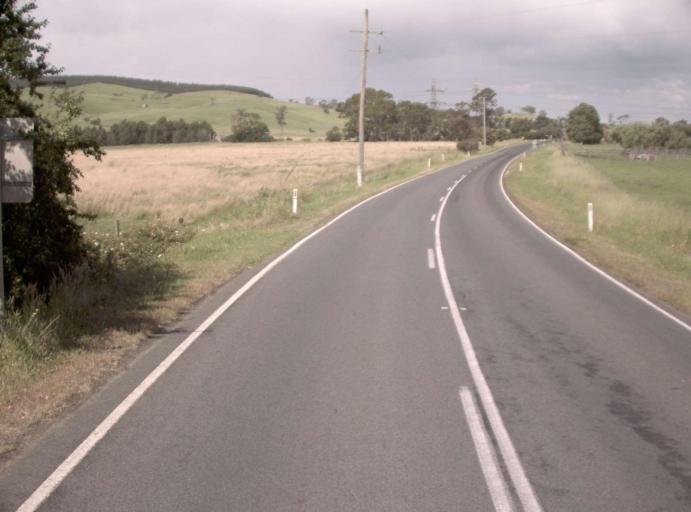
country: AU
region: Victoria
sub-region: Latrobe
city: Morwell
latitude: -38.1484
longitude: 146.4430
